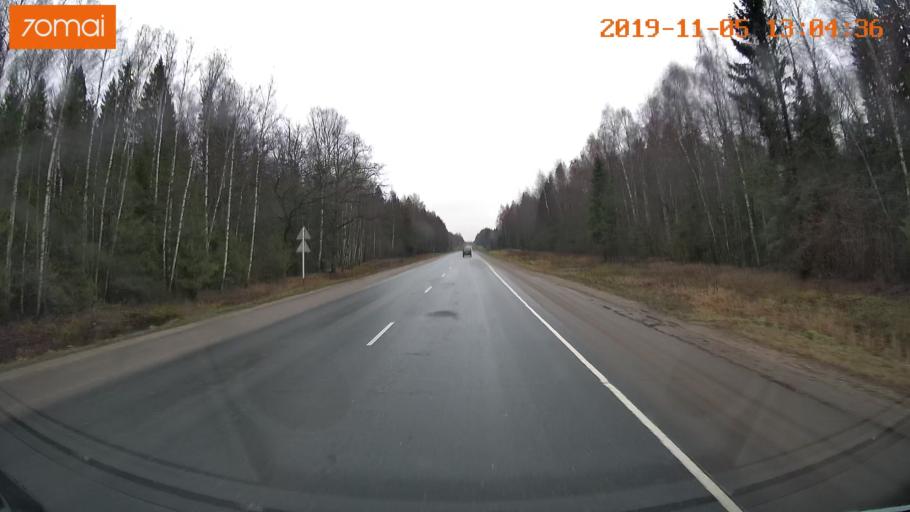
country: RU
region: Ivanovo
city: Kitovo
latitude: 56.8880
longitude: 41.2247
